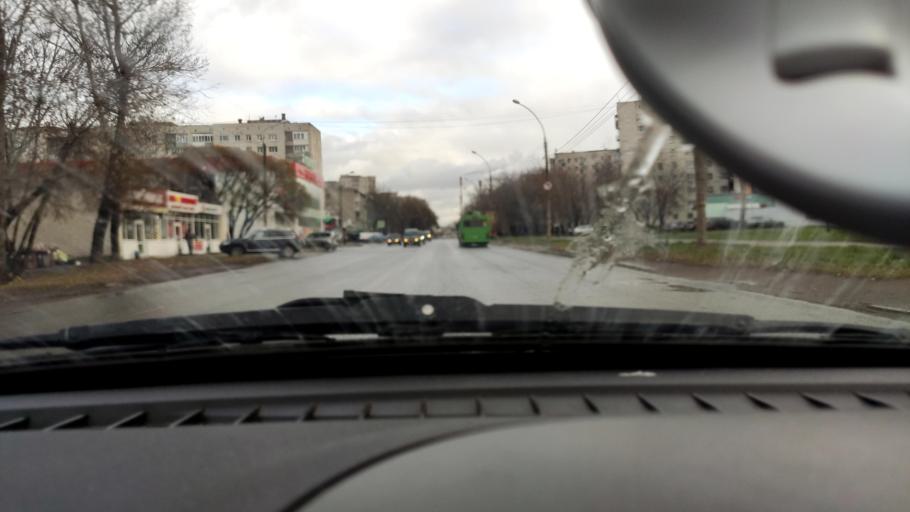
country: RU
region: Perm
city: Perm
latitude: 57.9718
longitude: 56.2344
